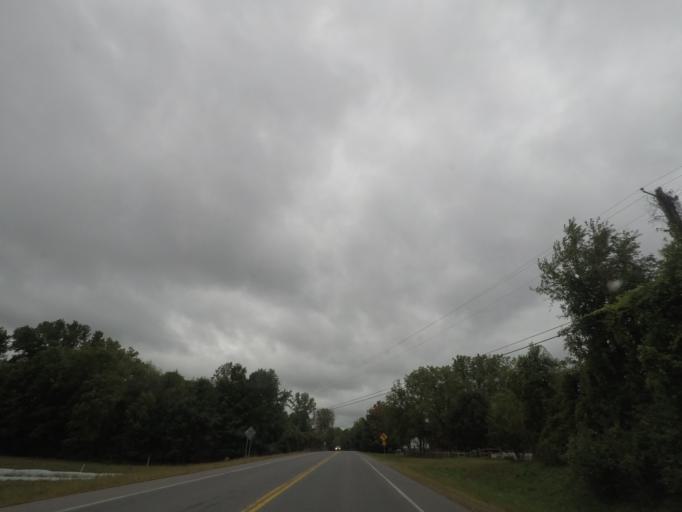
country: US
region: New York
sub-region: Saratoga County
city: Mechanicville
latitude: 42.8986
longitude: -73.6713
